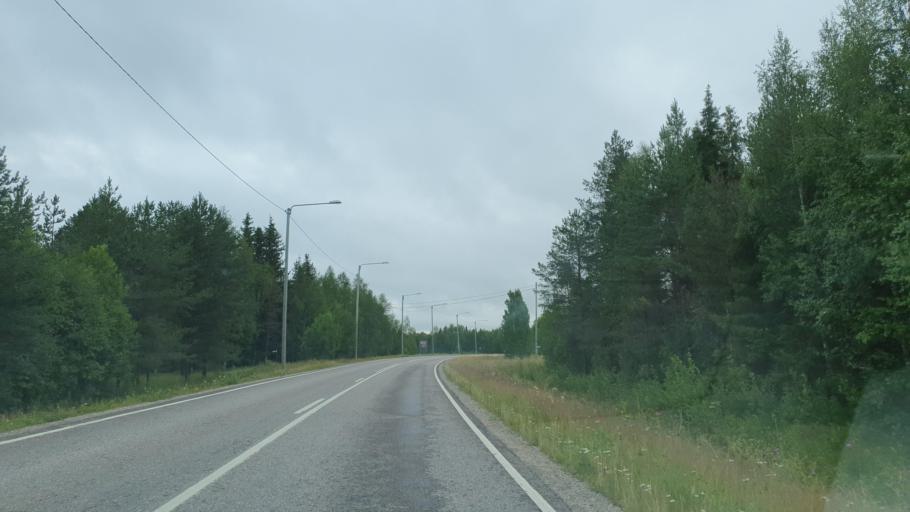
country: FI
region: Lapland
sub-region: Itae-Lappi
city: Pelkosenniemi
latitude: 66.9812
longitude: 27.5281
